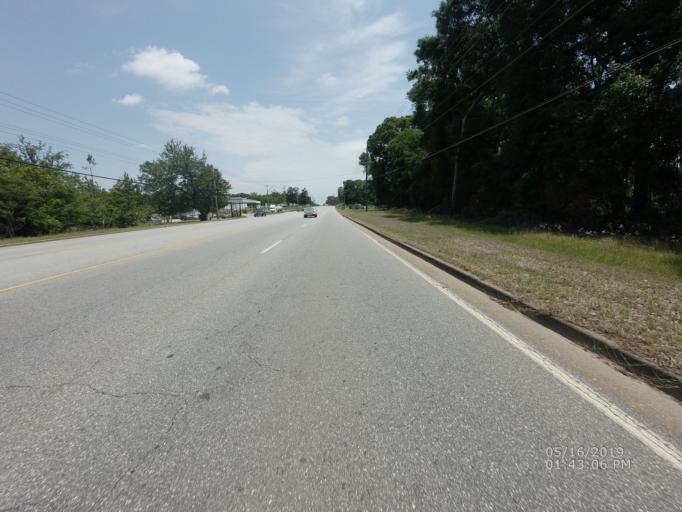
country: US
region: Georgia
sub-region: Dougherty County
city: Albany
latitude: 31.5490
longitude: -84.2024
